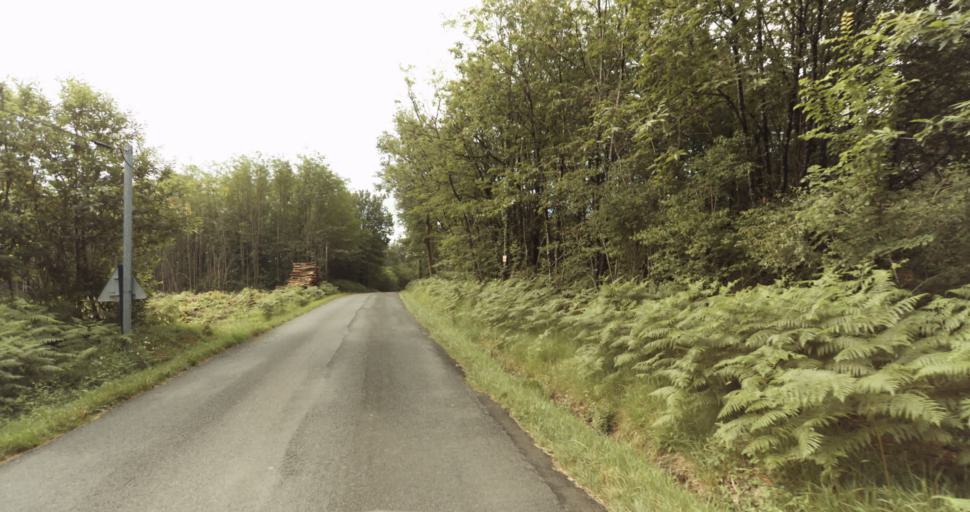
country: FR
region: Aquitaine
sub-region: Departement de la Dordogne
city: Le Bugue
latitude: 44.9307
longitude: 0.8188
